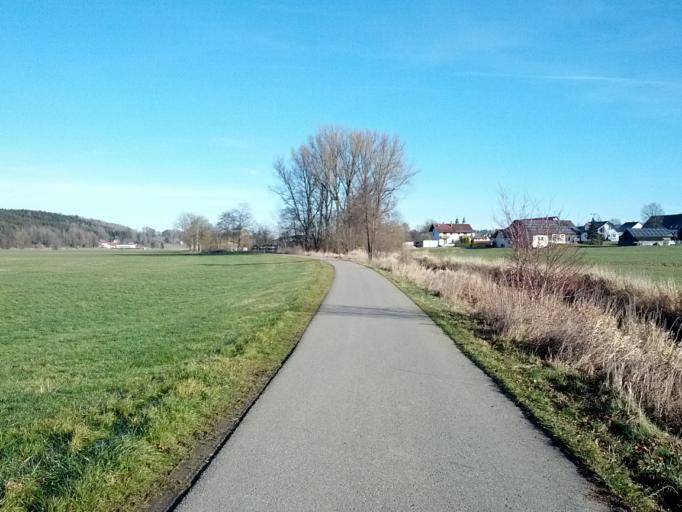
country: DE
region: Baden-Wuerttemberg
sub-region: Tuebingen Region
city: Rot an der Rot
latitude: 48.0080
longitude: 10.0165
